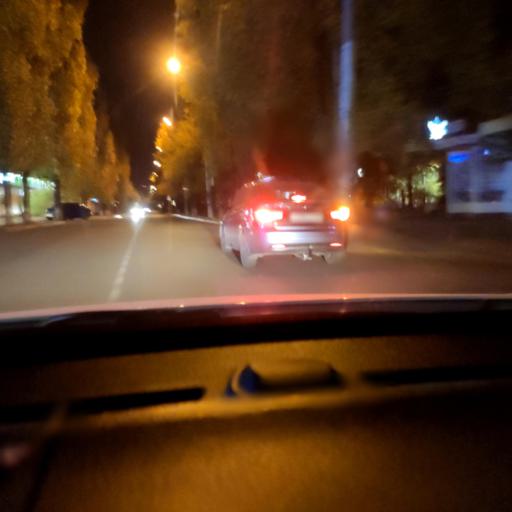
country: RU
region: Voronezj
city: Voronezh
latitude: 51.6888
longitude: 39.2596
